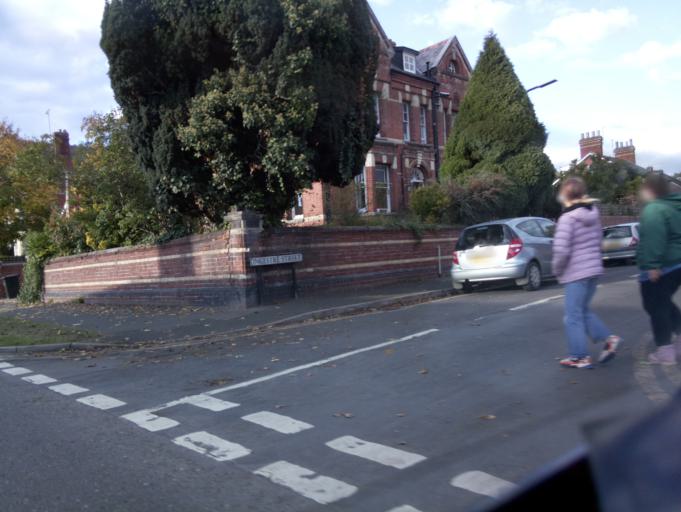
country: GB
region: England
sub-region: Herefordshire
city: Belmont
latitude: 52.0605
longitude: -2.7365
